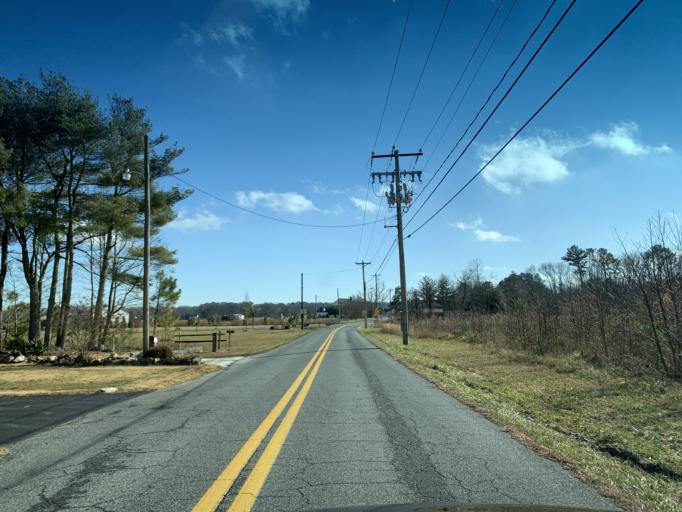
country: US
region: Delaware
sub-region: Sussex County
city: Selbyville
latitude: 38.4519
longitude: -75.1965
